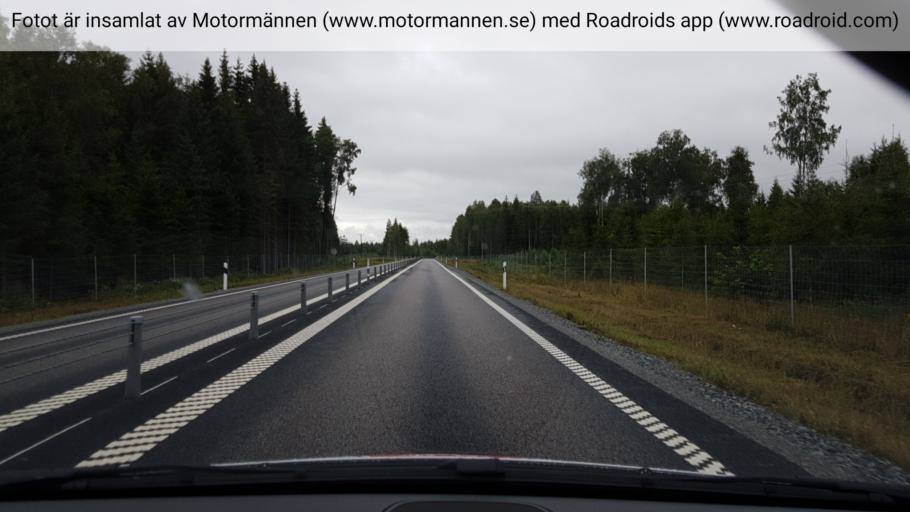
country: SE
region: Uppsala
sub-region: Heby Kommun
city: Heby
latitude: 60.0359
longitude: 16.8711
